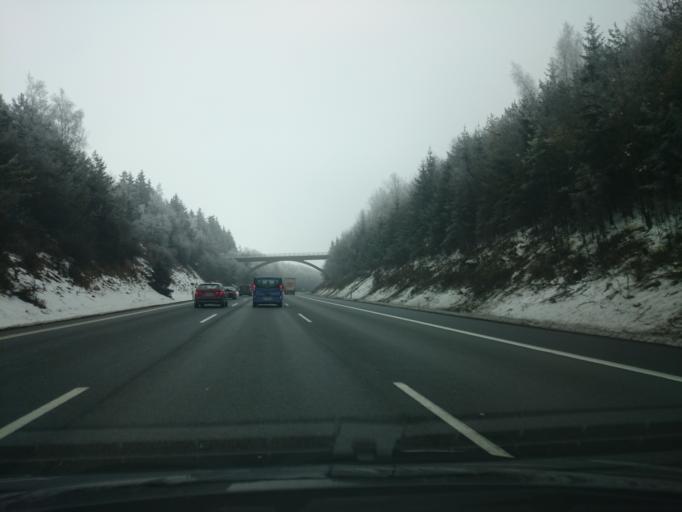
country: DE
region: Bavaria
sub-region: Upper Bavaria
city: Denkendorf
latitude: 48.9666
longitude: 11.4104
